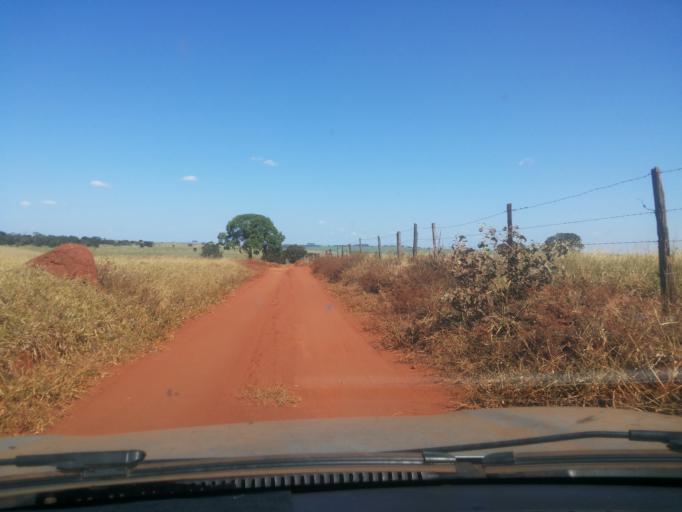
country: BR
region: Minas Gerais
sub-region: Centralina
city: Centralina
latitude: -18.7495
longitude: -49.1877
